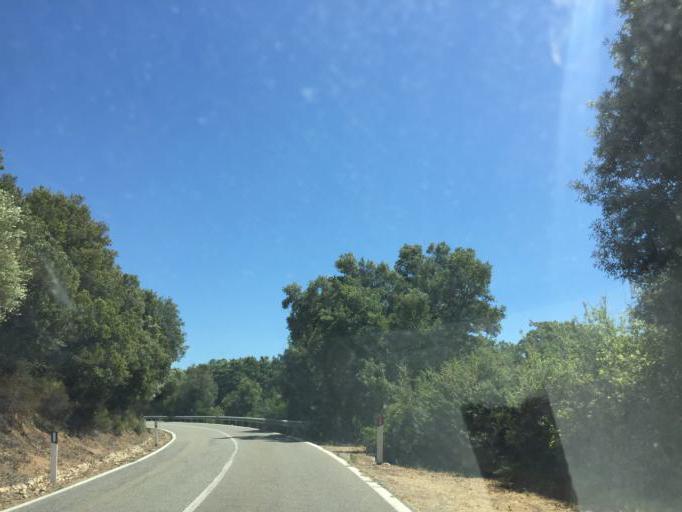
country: IT
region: Sardinia
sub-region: Provincia di Olbia-Tempio
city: Telti
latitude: 40.8962
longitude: 9.2777
